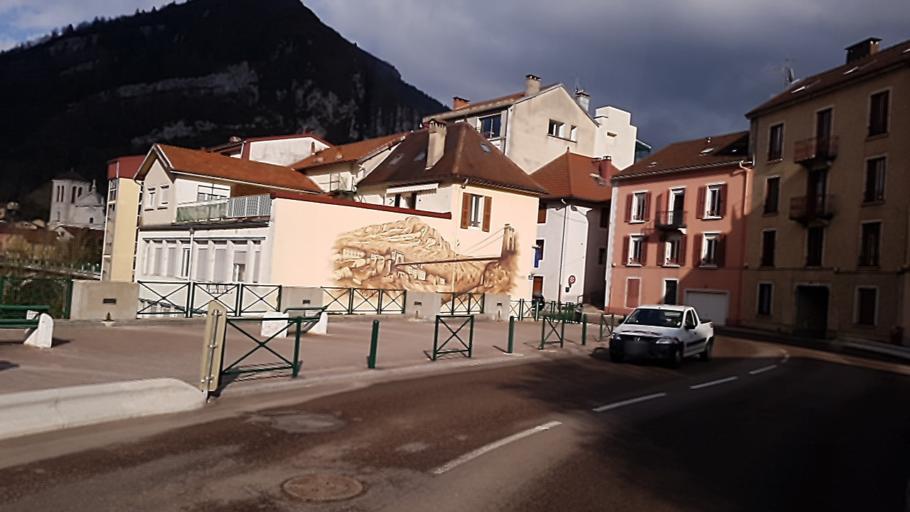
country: FR
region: Franche-Comte
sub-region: Departement du Jura
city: Saint-Claude
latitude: 46.3840
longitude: 5.8628
